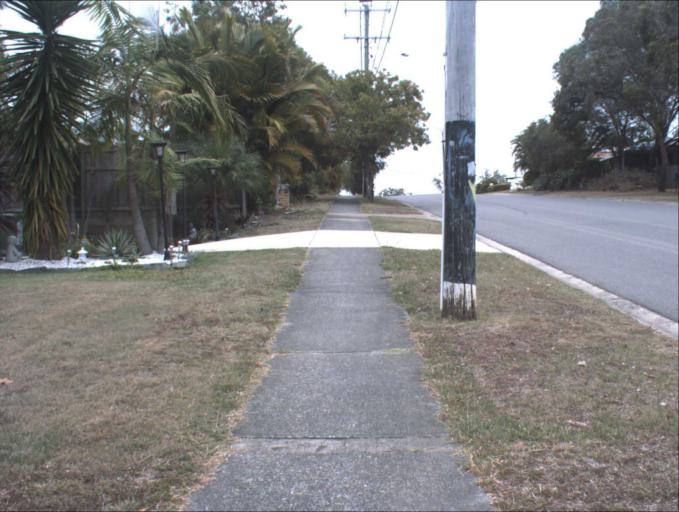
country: AU
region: Queensland
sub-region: Logan
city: Slacks Creek
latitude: -27.6493
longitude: 153.1656
